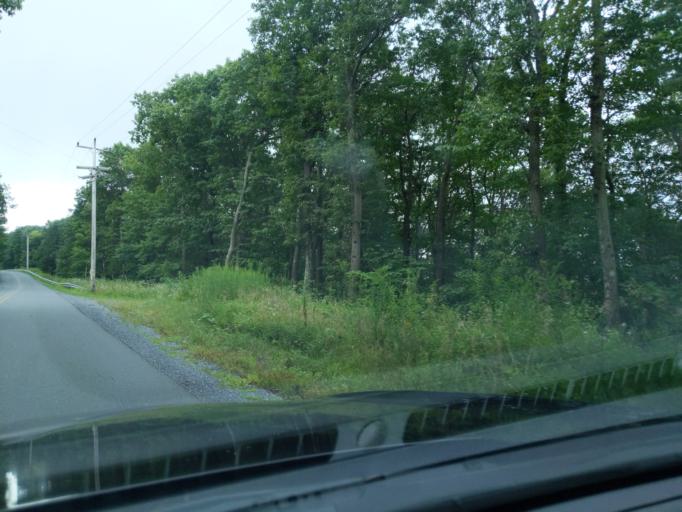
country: US
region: Pennsylvania
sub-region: Blair County
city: Claysburg
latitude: 40.2909
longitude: -78.5716
